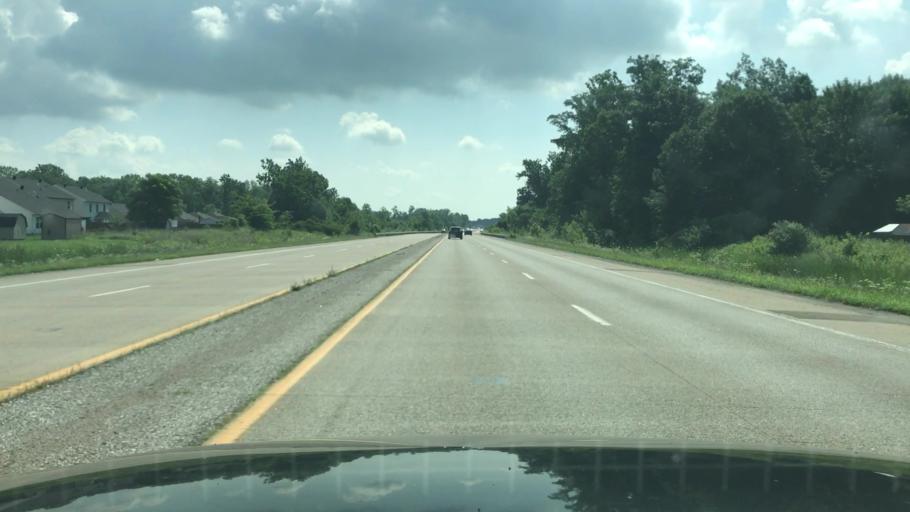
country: US
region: Indiana
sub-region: Vanderburgh County
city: Melody Hill
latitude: 38.0131
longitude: -87.5052
